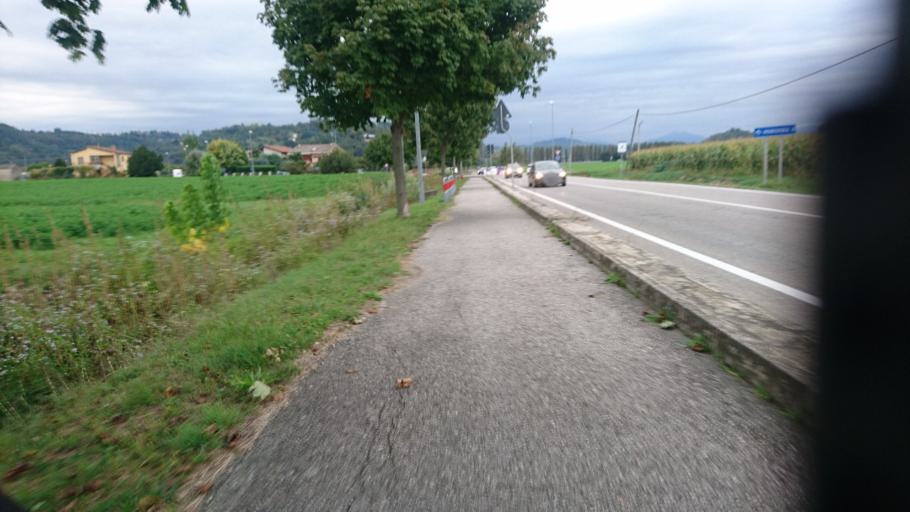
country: IT
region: Veneto
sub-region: Provincia di Vicenza
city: Creazzo
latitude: 45.5365
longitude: 11.4926
